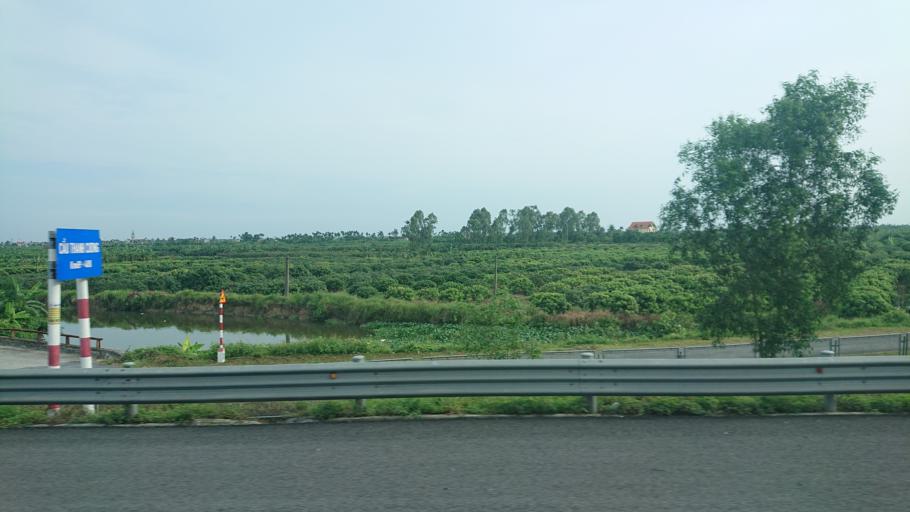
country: VN
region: Hai Phong
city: An Lao
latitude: 20.8189
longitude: 106.4824
